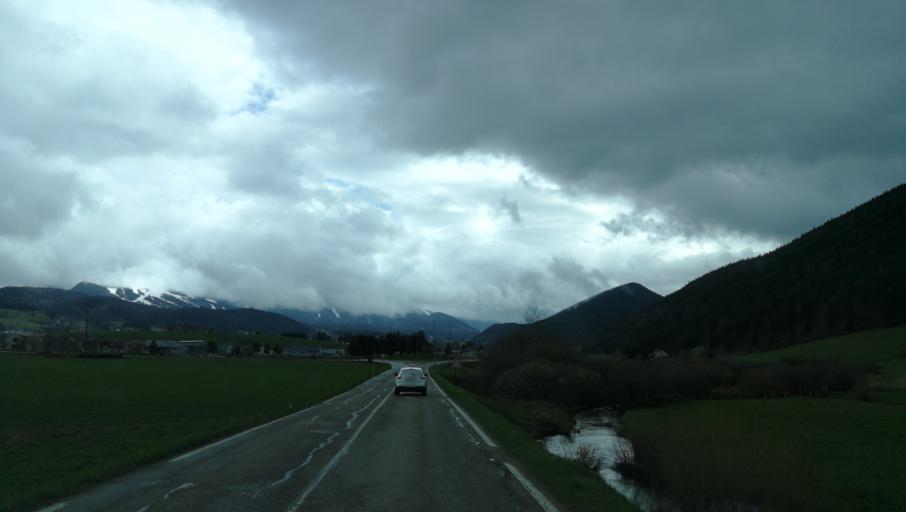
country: FR
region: Rhone-Alpes
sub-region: Departement de l'Isere
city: Villard-de-Lans
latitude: 45.0922
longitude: 5.5561
